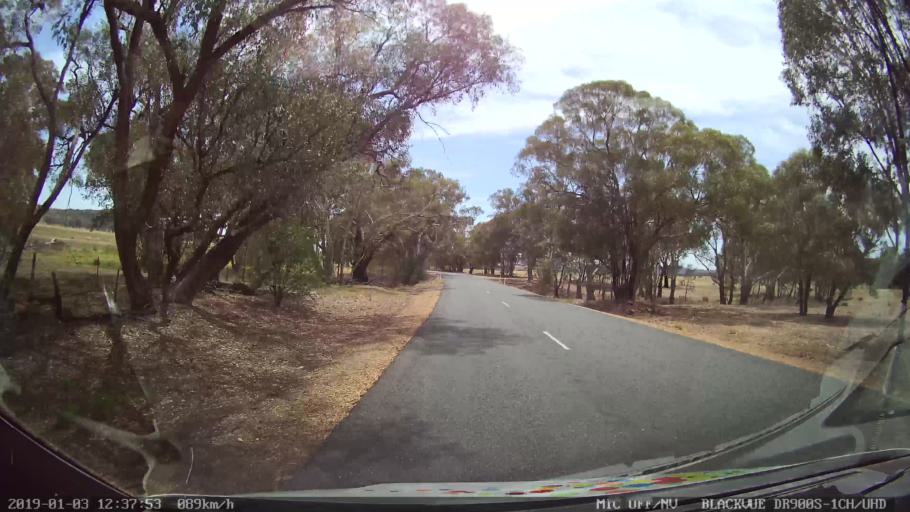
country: AU
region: New South Wales
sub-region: Weddin
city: Grenfell
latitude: -33.8387
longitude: 148.1894
